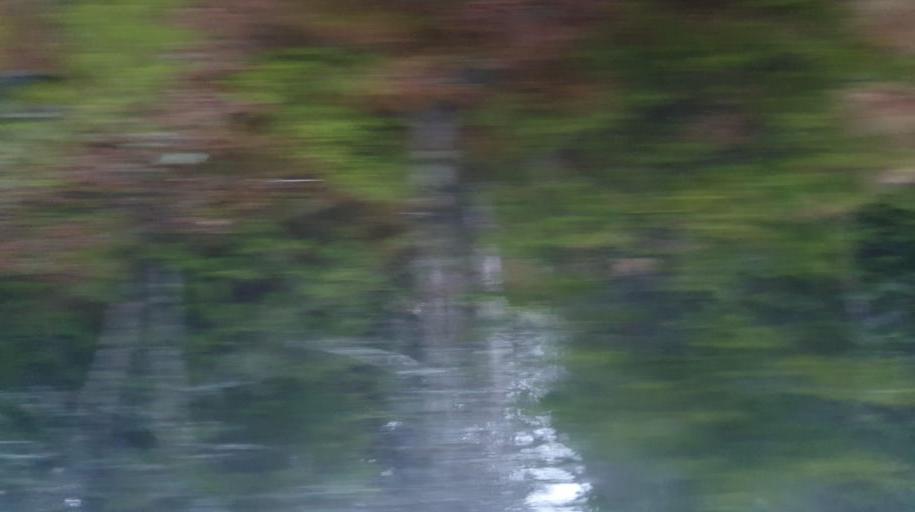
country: NO
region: Buskerud
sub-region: Krodsherad
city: Noresund
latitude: 60.2154
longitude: 9.5465
